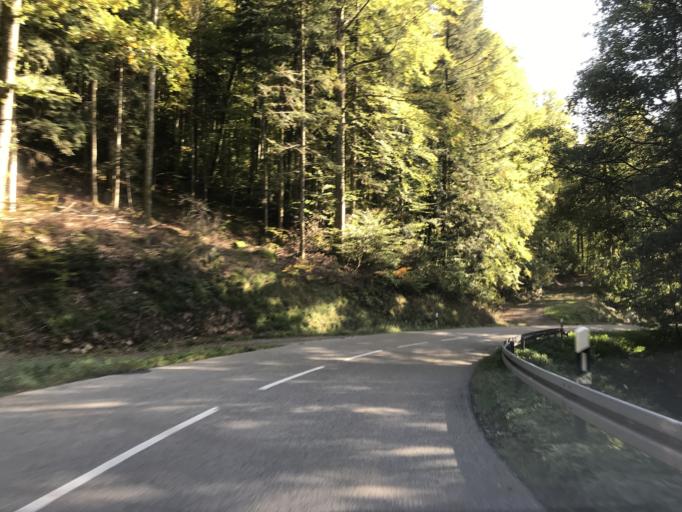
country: DE
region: Baden-Wuerttemberg
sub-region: Freiburg Region
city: Wehr
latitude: 47.6270
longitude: 7.9298
